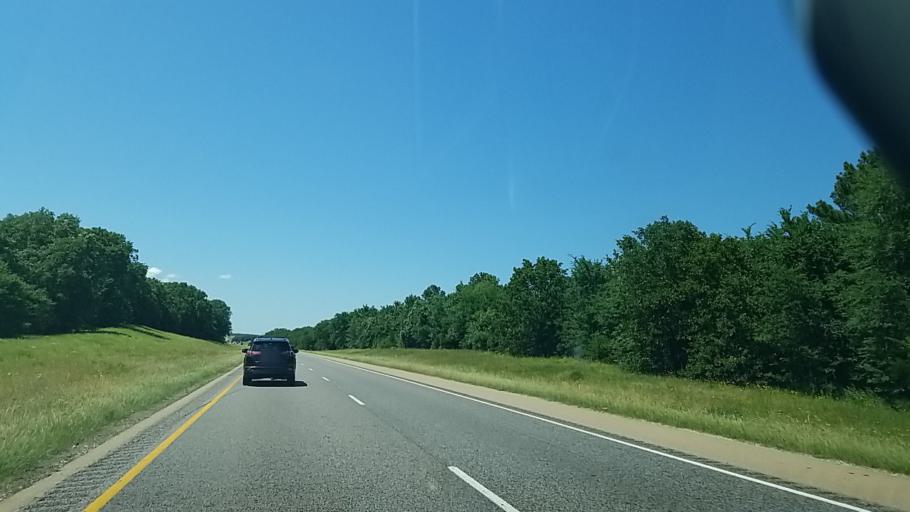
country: US
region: Texas
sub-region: Leon County
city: Buffalo
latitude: 31.5509
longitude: -96.1285
